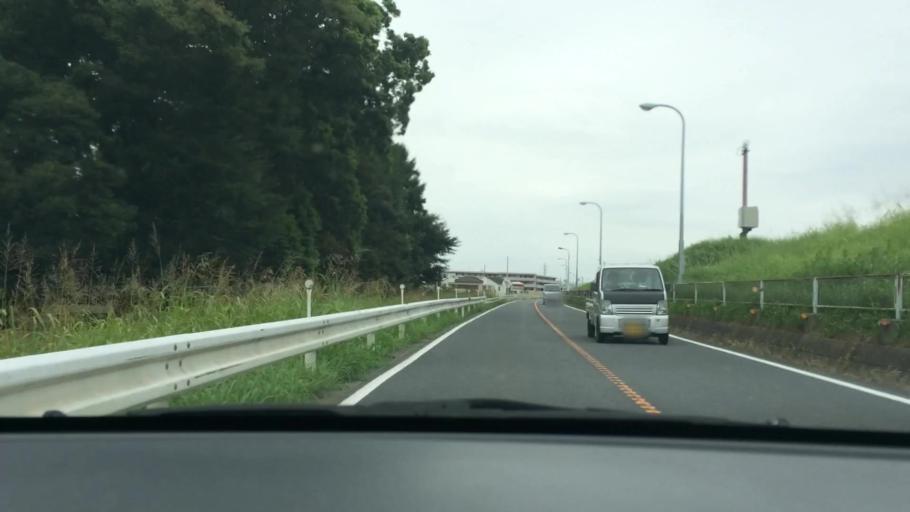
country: JP
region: Chiba
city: Matsudo
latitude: 35.7704
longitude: 139.8785
